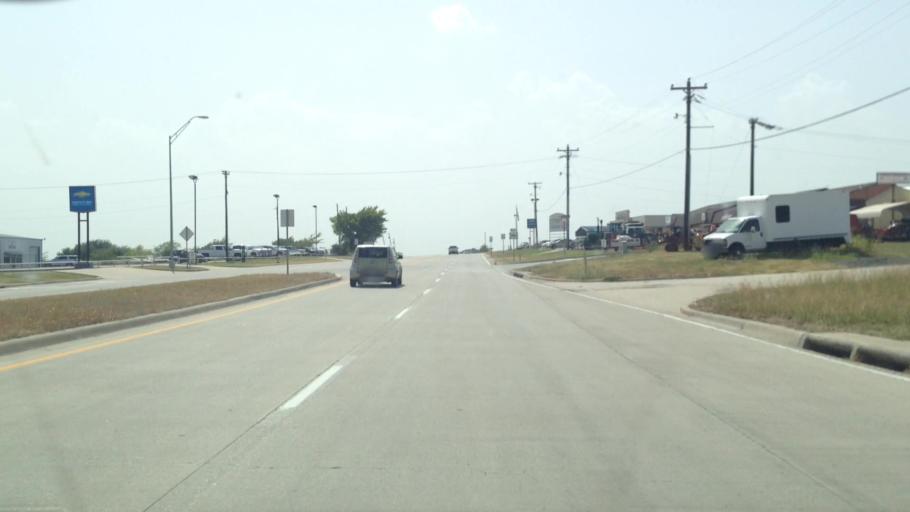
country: US
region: Texas
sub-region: Collin County
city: Farmersville
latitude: 33.1583
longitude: -96.3785
